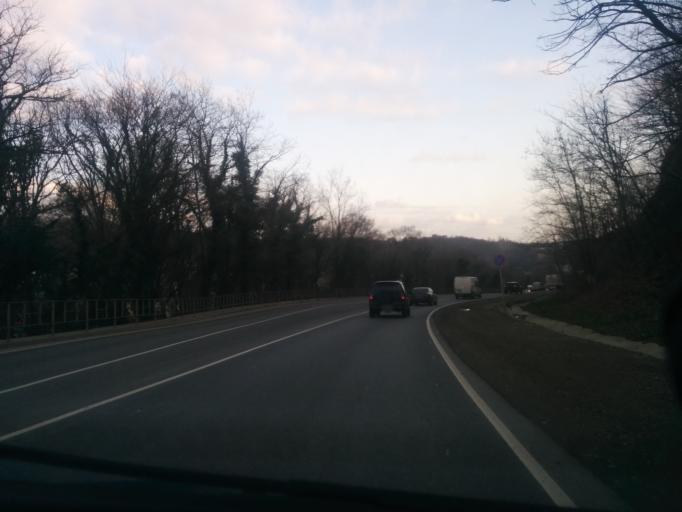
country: RU
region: Krasnodarskiy
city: Tuapse
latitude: 44.1177
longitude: 39.0533
